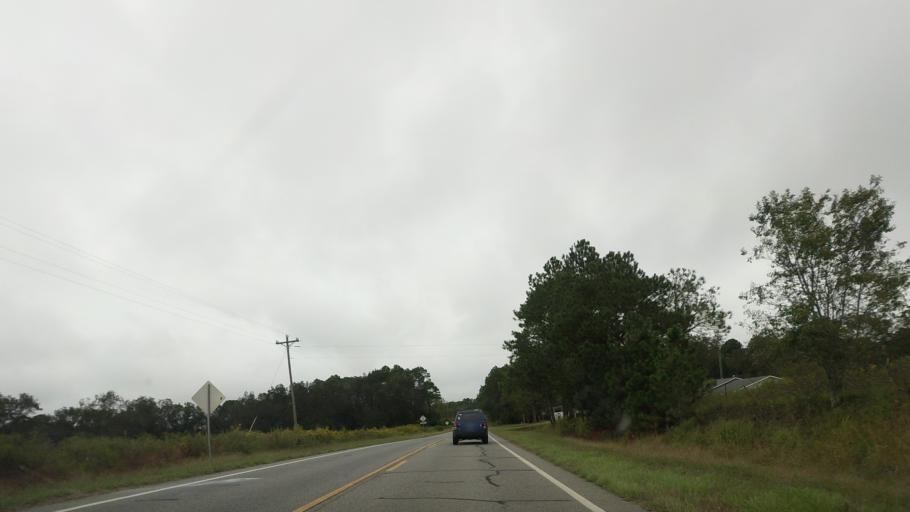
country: US
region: Georgia
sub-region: Irwin County
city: Ocilla
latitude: 31.5422
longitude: -83.2536
